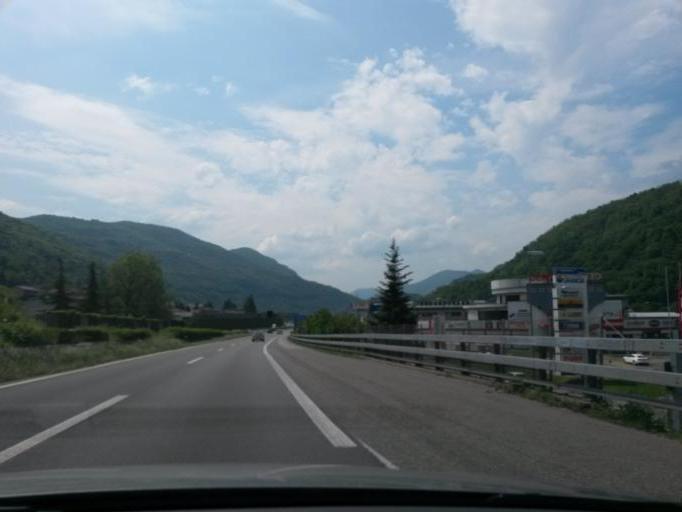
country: CH
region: Ticino
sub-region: Lugano District
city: Montagnola
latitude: 45.9732
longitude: 8.9285
